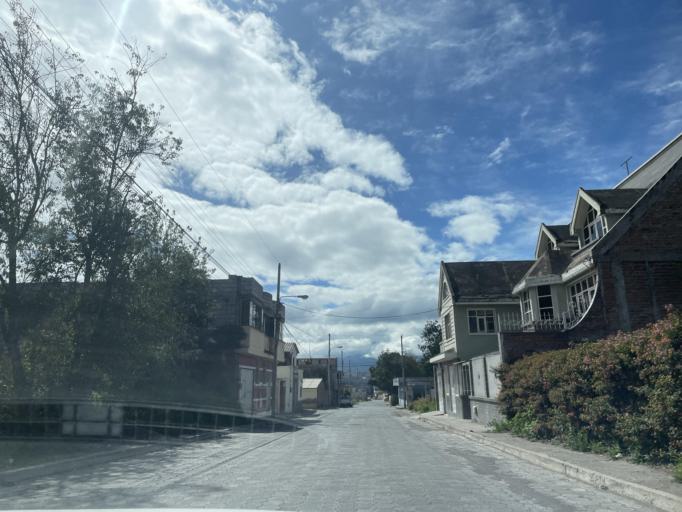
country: EC
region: Chimborazo
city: Guano
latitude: -1.6070
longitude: -78.6339
